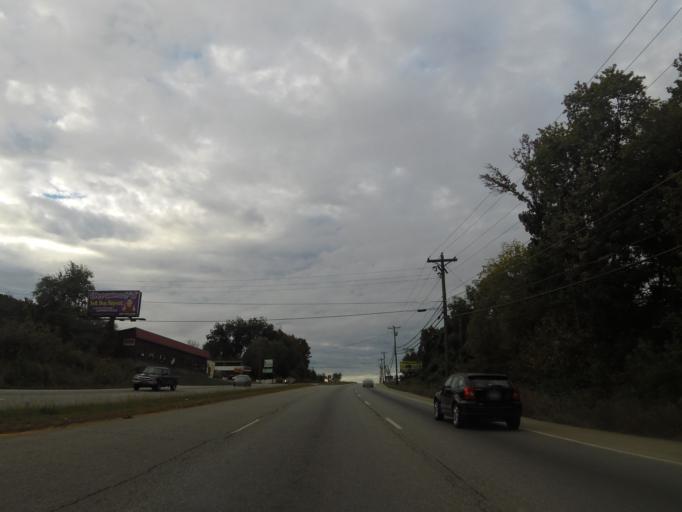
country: US
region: Tennessee
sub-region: Blount County
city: Eagleton Village
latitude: 35.8568
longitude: -83.9603
